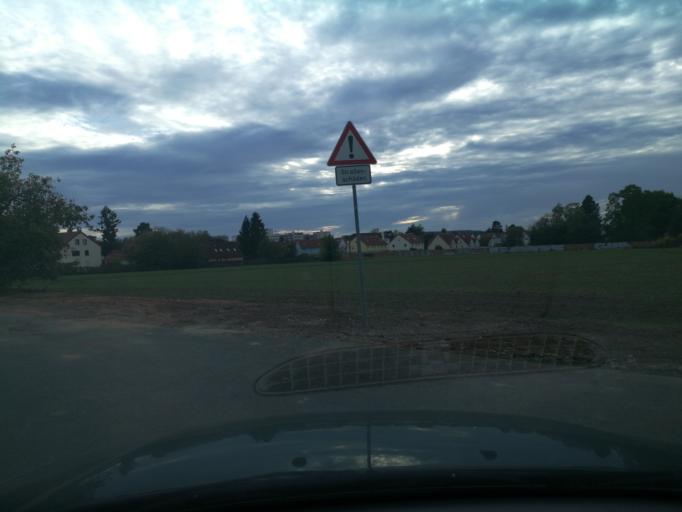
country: DE
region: Bavaria
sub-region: Regierungsbezirk Mittelfranken
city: Furth
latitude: 49.4879
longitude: 10.9684
